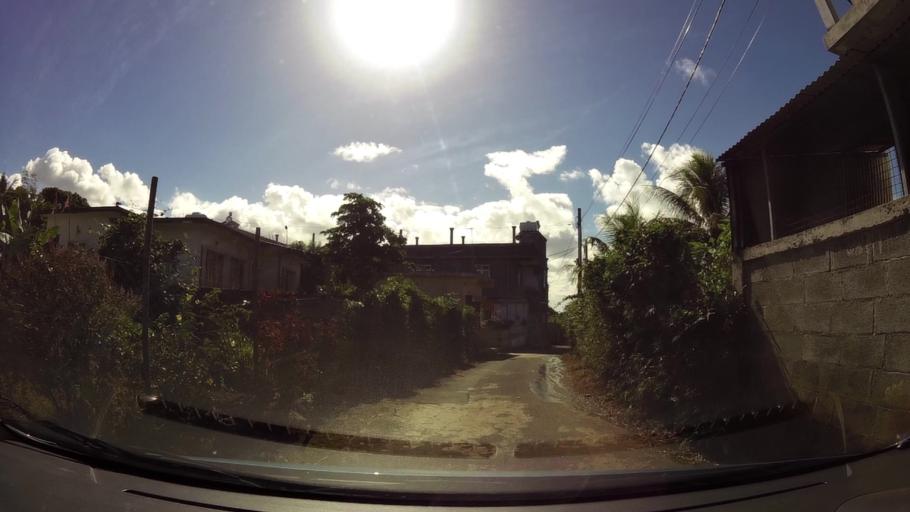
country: MU
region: Grand Port
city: Mahebourg
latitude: -20.3993
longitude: 57.6943
